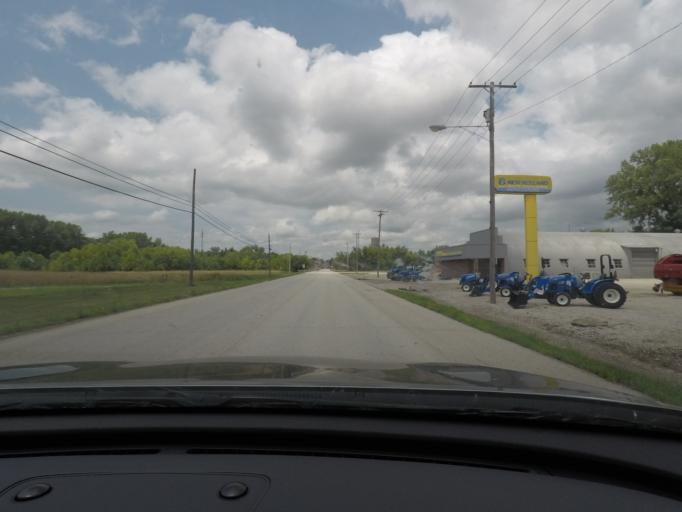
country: US
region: Missouri
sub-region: Carroll County
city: Carrollton
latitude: 39.3452
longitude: -93.4959
